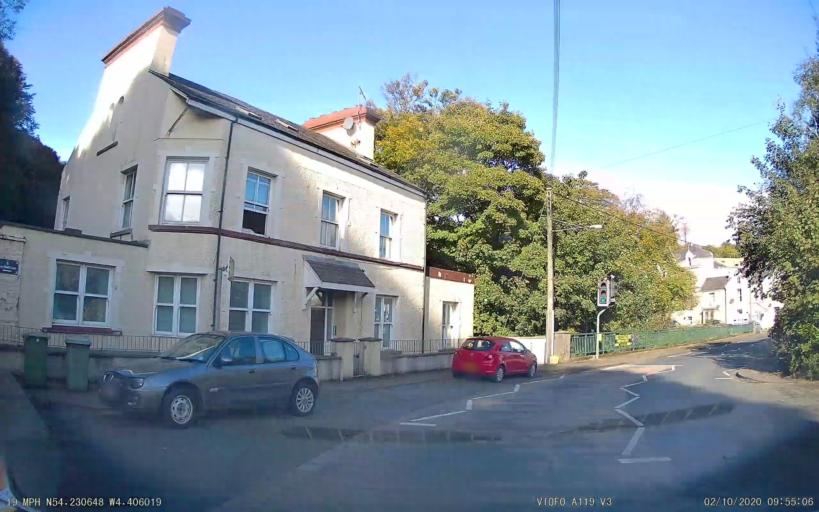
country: IM
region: Laxey
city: Laxey
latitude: 54.2307
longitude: -4.4059
